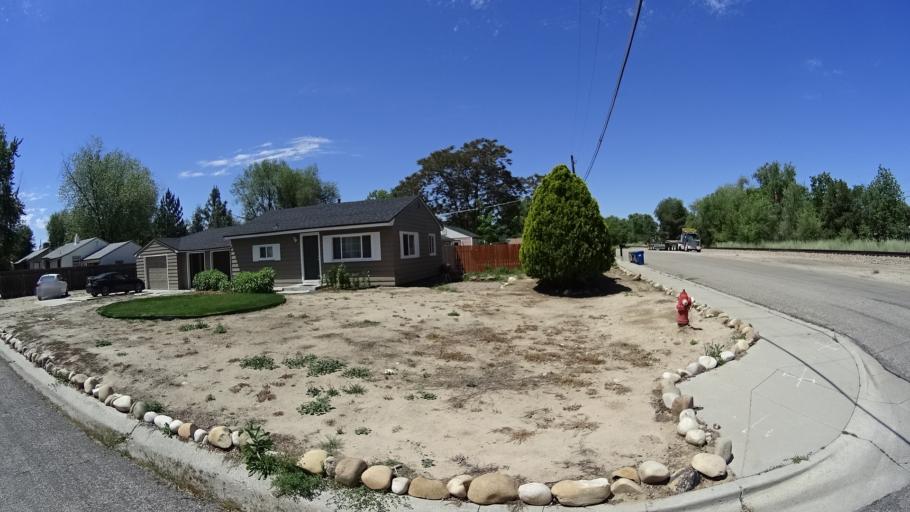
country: US
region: Idaho
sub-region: Ada County
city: Boise
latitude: 43.6043
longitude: -116.2236
